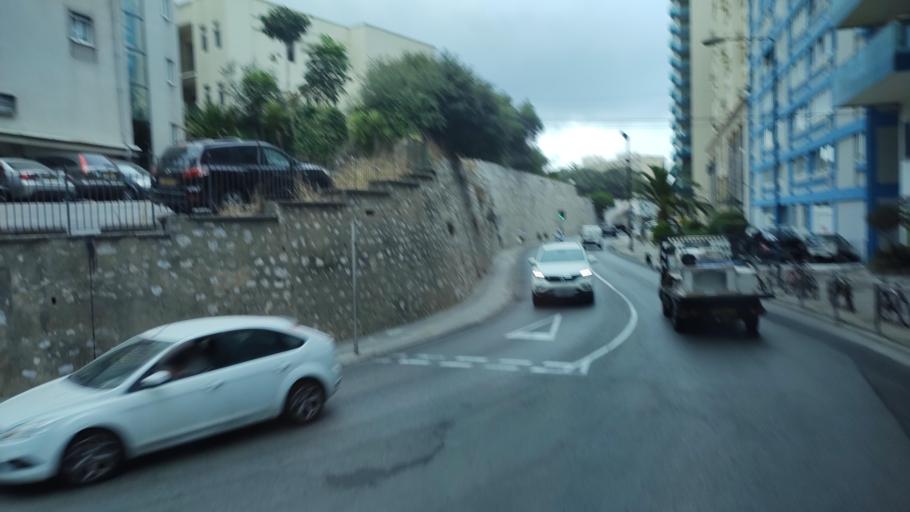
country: GI
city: Gibraltar
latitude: 36.1472
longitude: -5.3526
